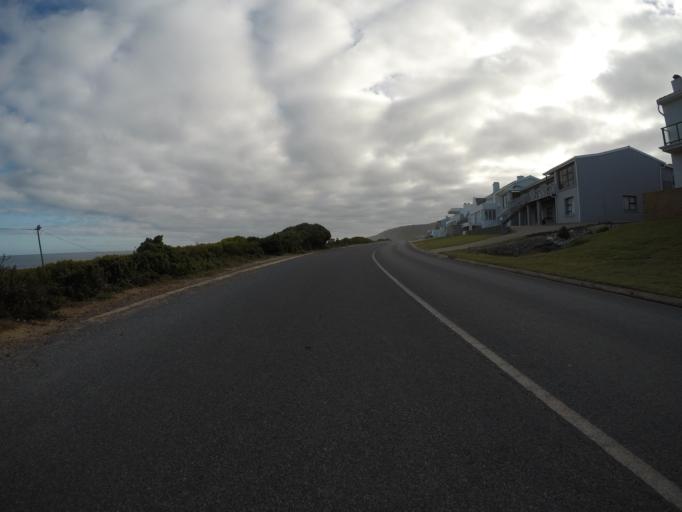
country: ZA
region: Western Cape
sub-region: Eden District Municipality
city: Riversdale
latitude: -34.4329
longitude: 21.3330
